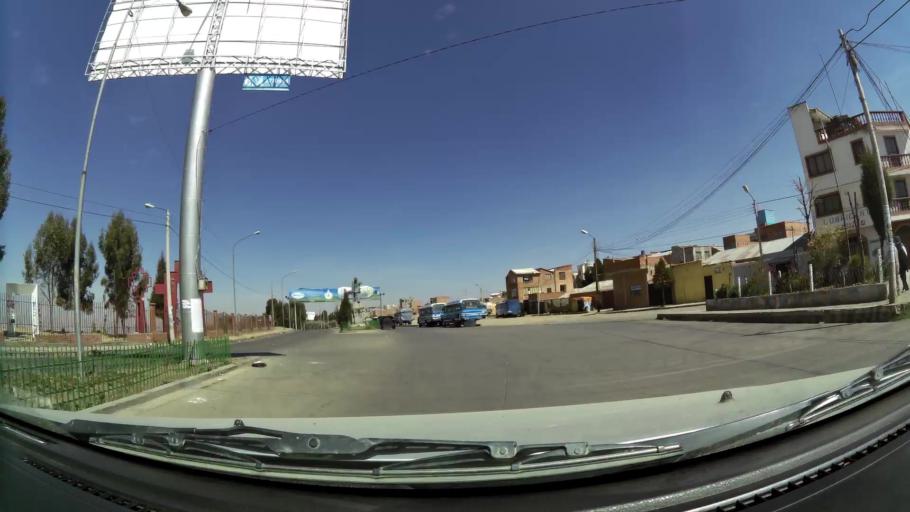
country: BO
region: La Paz
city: La Paz
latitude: -16.5299
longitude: -68.1471
